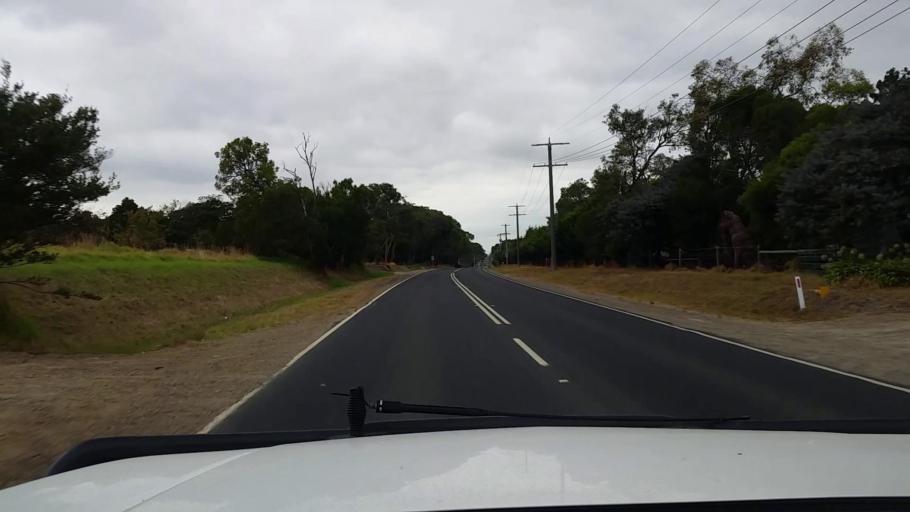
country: AU
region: Victoria
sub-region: Mornington Peninsula
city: Langwarrin South
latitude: -38.1999
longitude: 145.2093
